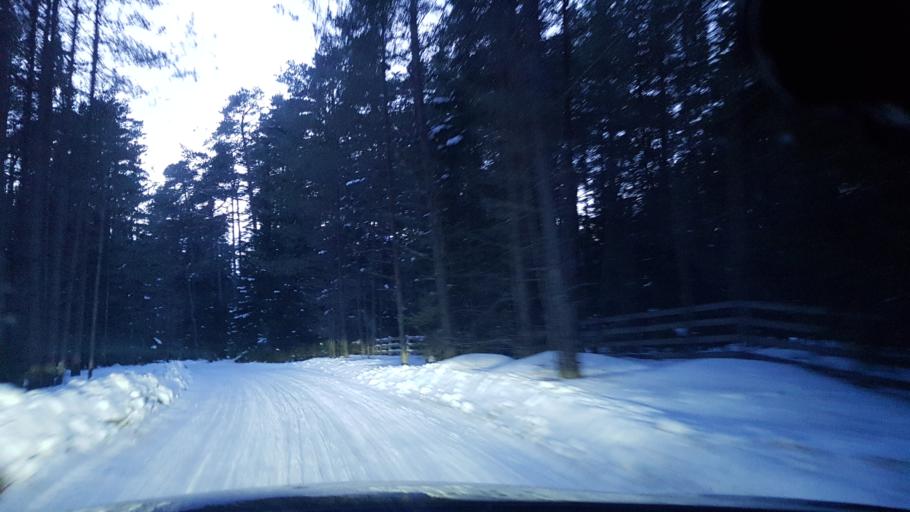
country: EE
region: Laeaene
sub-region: Haapsalu linn
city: Haapsalu
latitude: 59.2120
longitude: 23.5469
